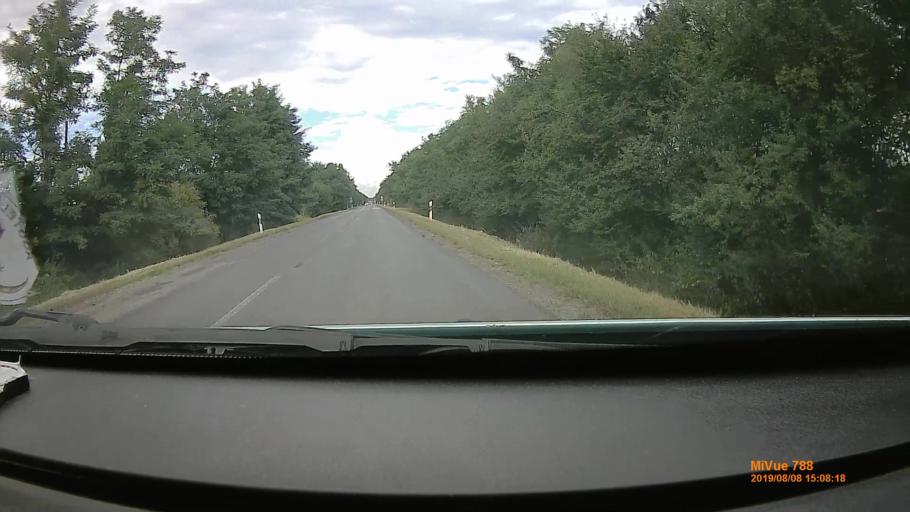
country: HU
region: Szabolcs-Szatmar-Bereg
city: Tunyogmatolcs
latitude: 47.9557
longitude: 22.4383
